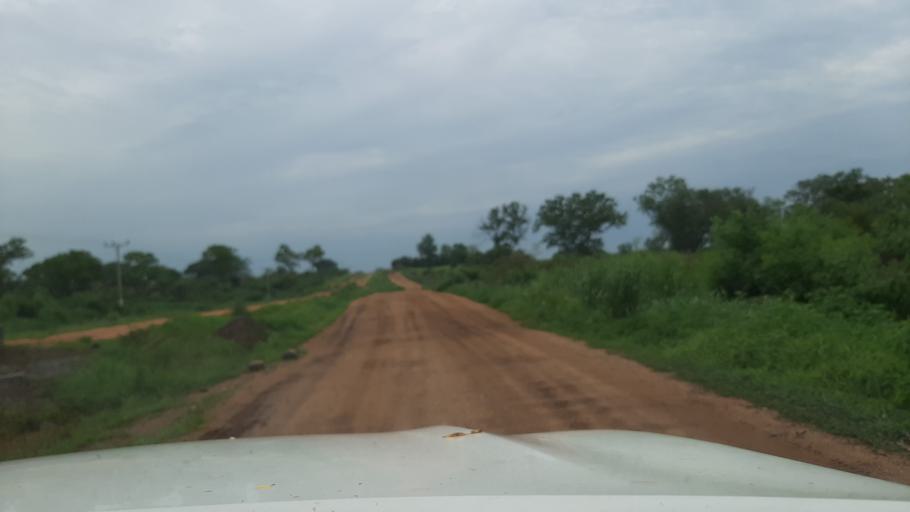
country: ET
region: Gambela
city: Gambela
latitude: 8.2197
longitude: 34.5435
